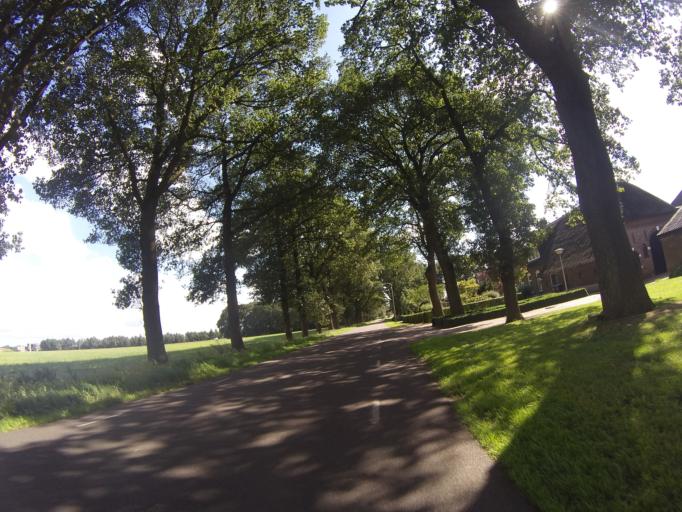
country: NL
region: Drenthe
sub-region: Gemeente Coevorden
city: Dalen
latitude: 52.7136
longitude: 6.7542
